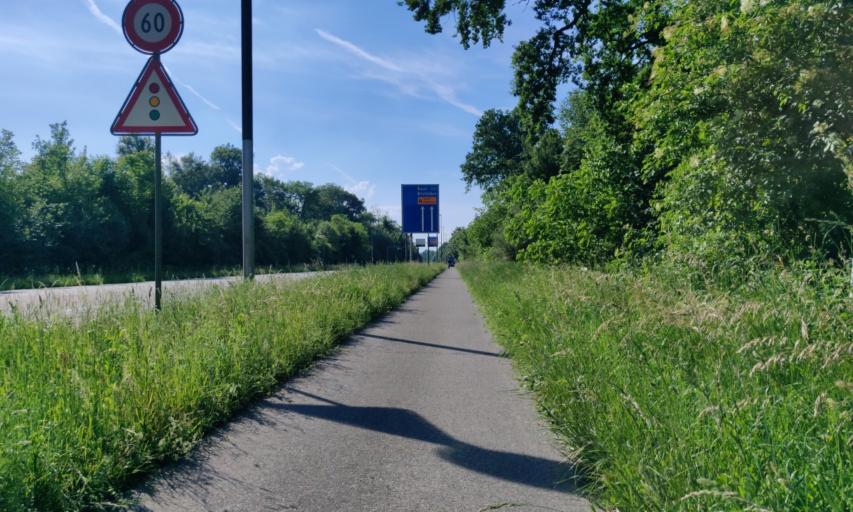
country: CH
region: Basel-Landschaft
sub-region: Bezirk Arlesheim
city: Muttenz
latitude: 47.5409
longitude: 7.6532
